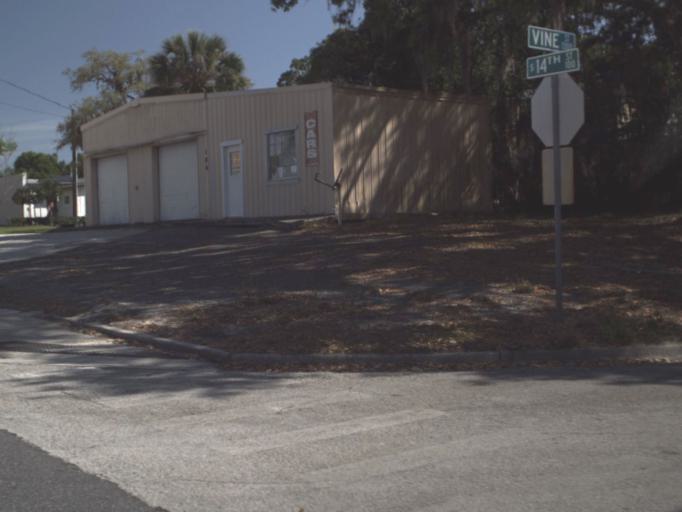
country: US
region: Florida
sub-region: Lake County
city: Leesburg
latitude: 28.8103
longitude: -81.8875
